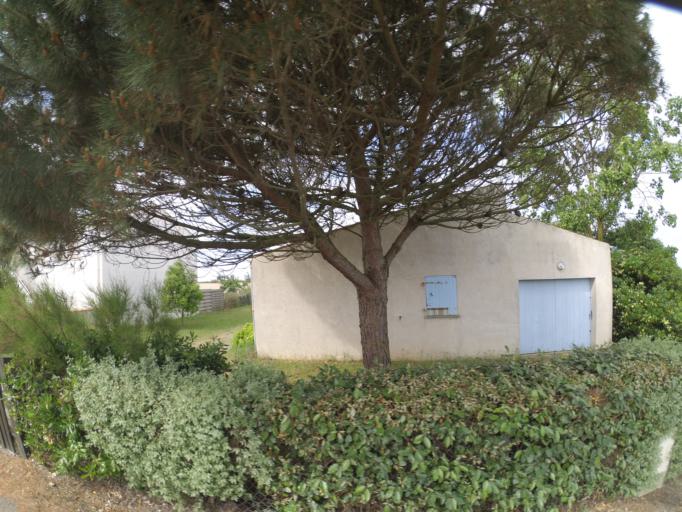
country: FR
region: Poitou-Charentes
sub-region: Departement de la Charente-Maritime
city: Angoulins
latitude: 46.0889
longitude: -1.0977
